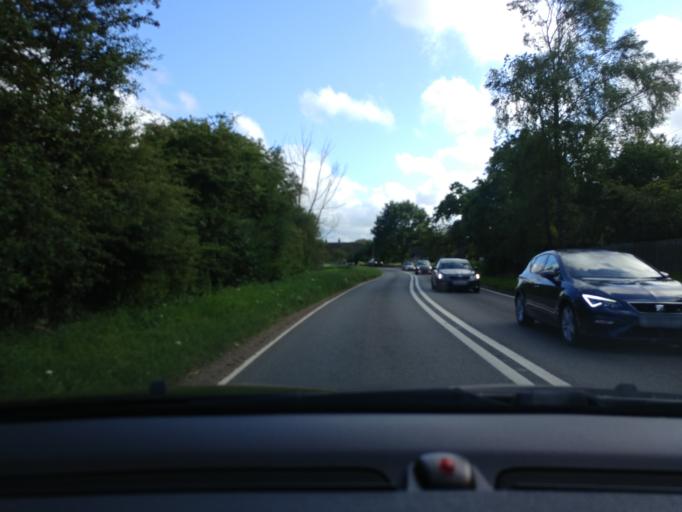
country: GB
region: England
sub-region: Oxfordshire
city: Kidlington
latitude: 51.8675
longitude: -1.2270
